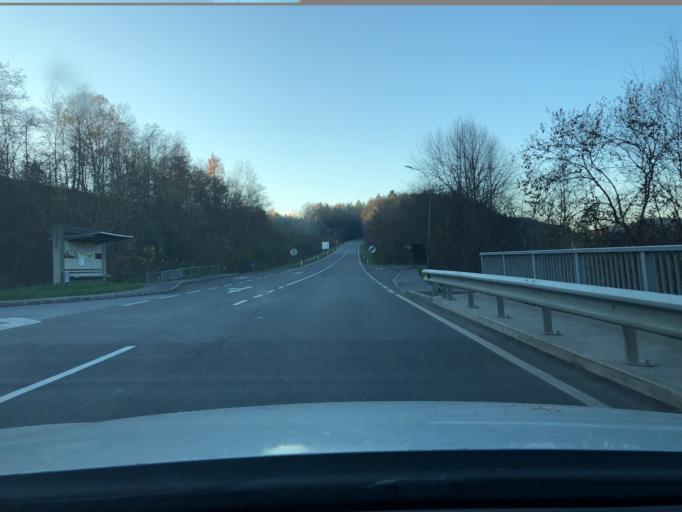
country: AT
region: Styria
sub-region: Politischer Bezirk Weiz
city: Sinabelkirchen
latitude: 47.1007
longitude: 15.7921
